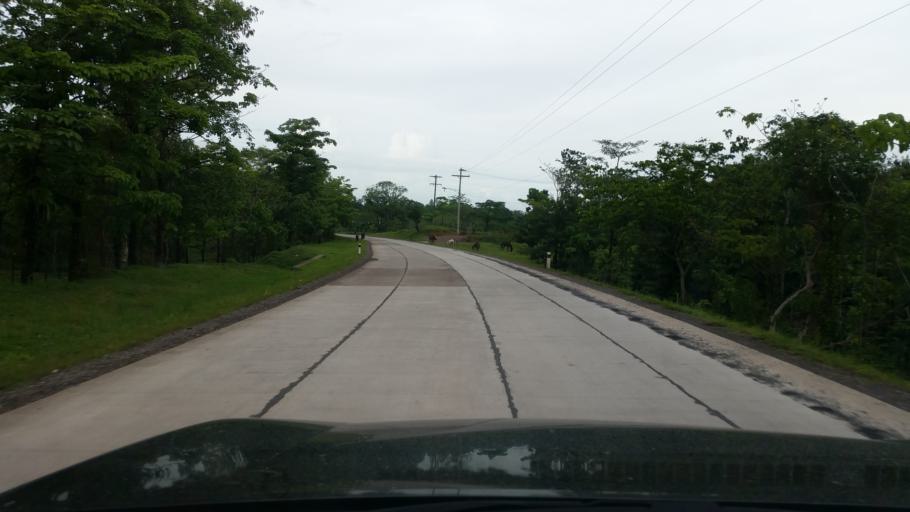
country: NI
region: Matagalpa
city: Rio Blanco
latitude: 13.1583
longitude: -84.9707
